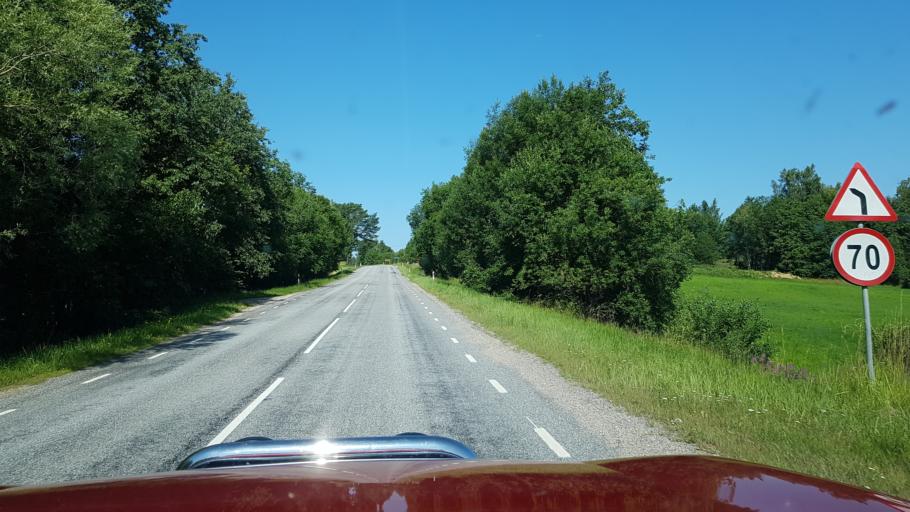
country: EE
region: Polvamaa
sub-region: Polva linn
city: Polva
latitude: 58.0887
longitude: 26.8247
